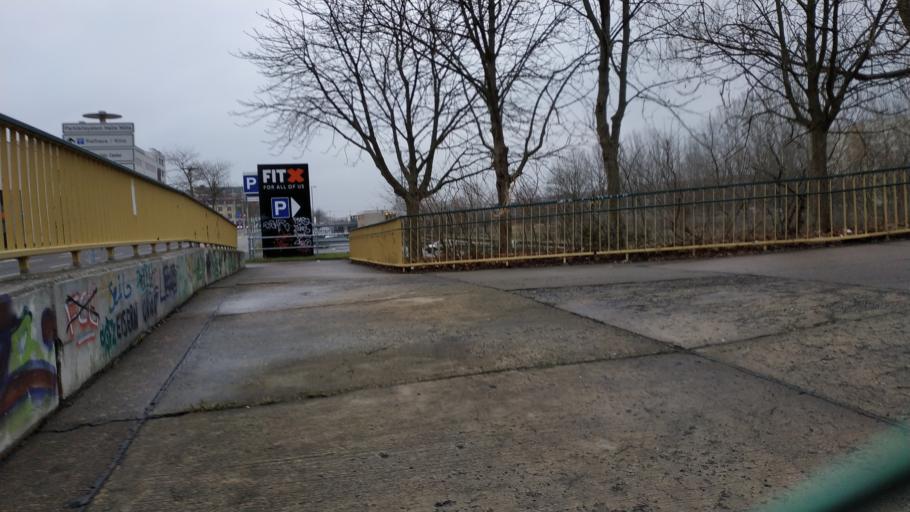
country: DE
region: Berlin
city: Hellersdorf
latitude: 52.5355
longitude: 13.6012
